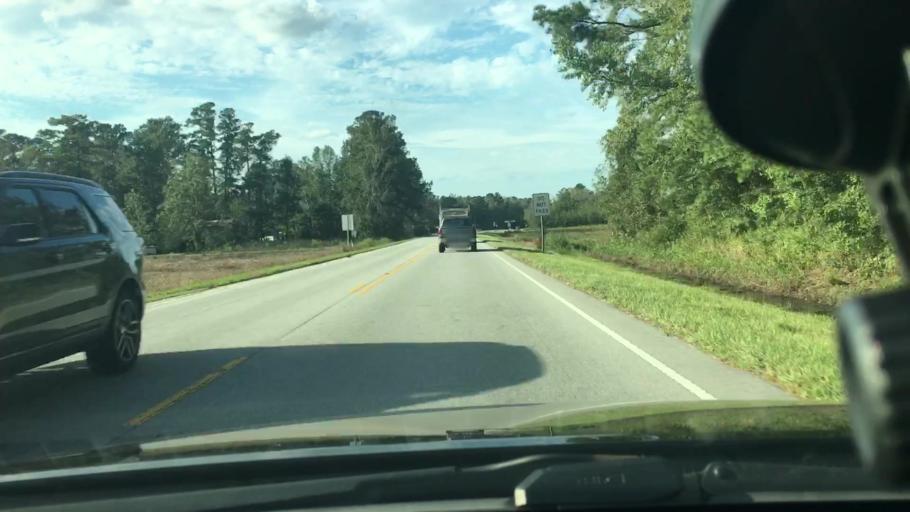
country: US
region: North Carolina
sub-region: Craven County
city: Vanceboro
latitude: 35.3297
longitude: -77.1493
